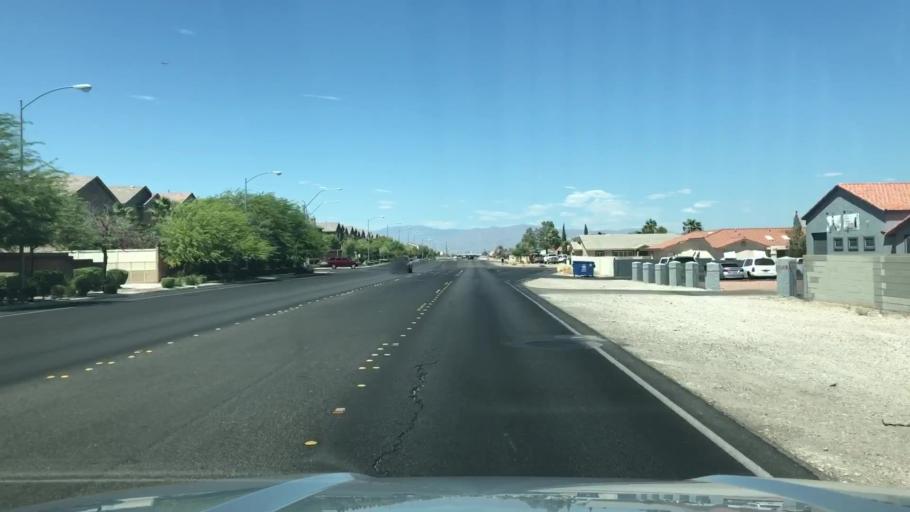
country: US
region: Nevada
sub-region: Clark County
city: Enterprise
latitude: 36.0487
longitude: -115.2078
